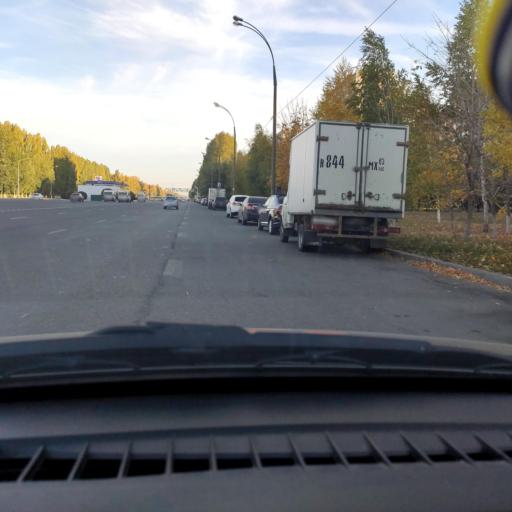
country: RU
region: Samara
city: Tol'yatti
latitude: 53.5029
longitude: 49.2756
